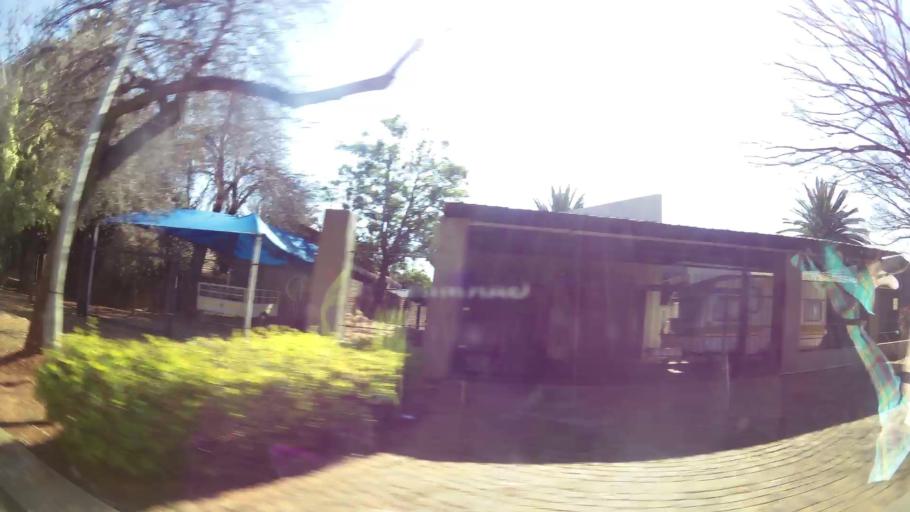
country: ZA
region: Gauteng
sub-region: City of Tshwane Metropolitan Municipality
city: Centurion
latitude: -25.8250
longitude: 28.2390
